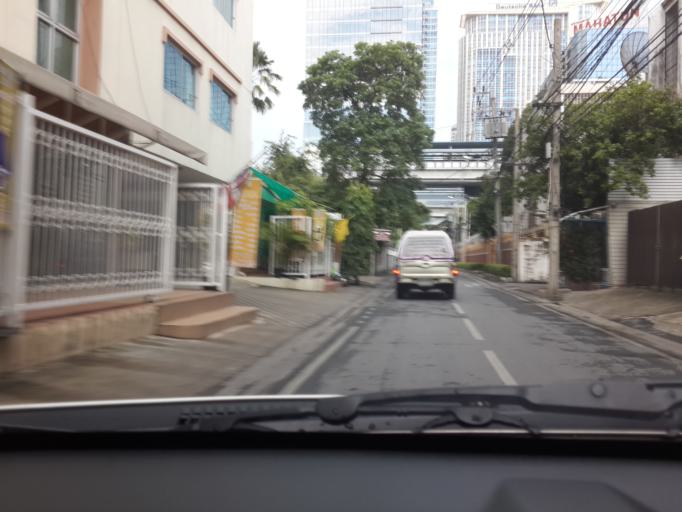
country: TH
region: Bangkok
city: Ratchathewi
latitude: 13.7442
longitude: 100.5497
